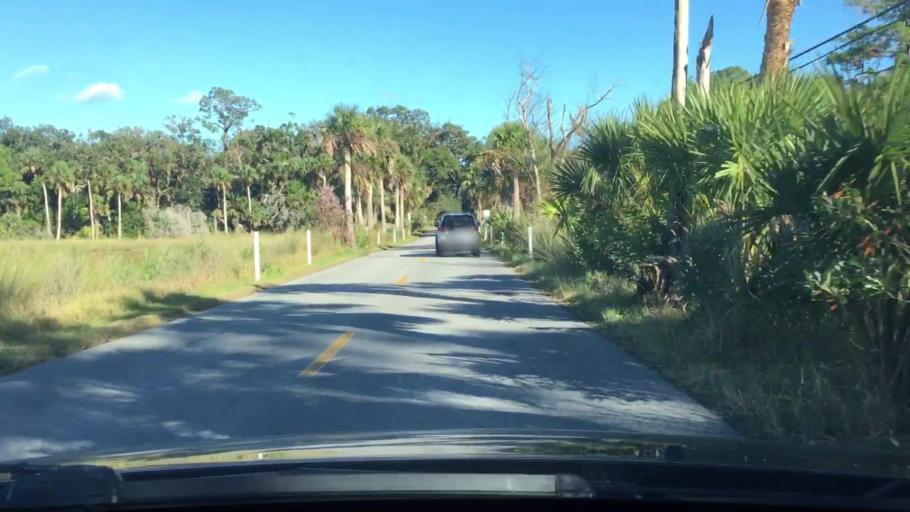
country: US
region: Florida
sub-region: Flagler County
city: Flagler Beach
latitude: 29.4061
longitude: -81.1269
